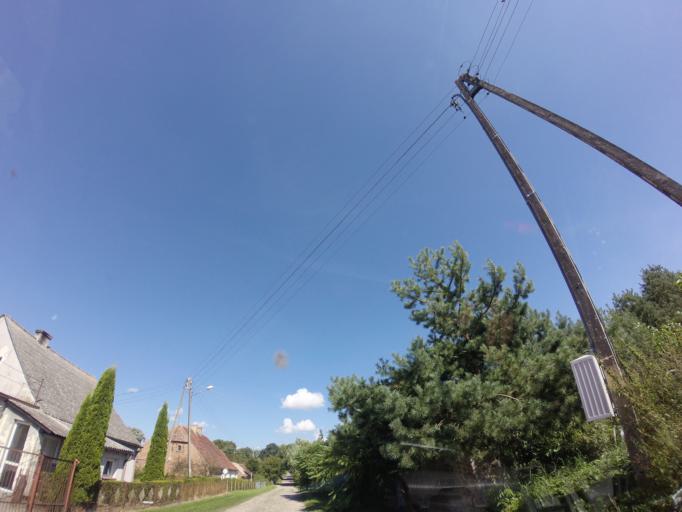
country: PL
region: West Pomeranian Voivodeship
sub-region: Powiat choszczenski
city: Recz
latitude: 53.1740
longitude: 15.5840
